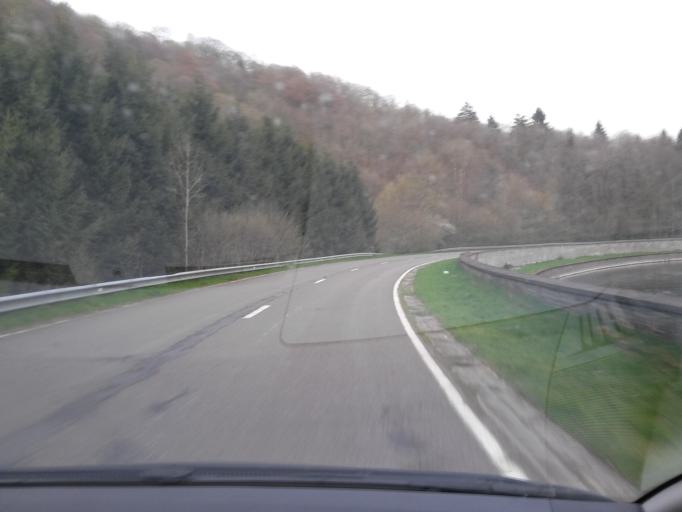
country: BE
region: Wallonia
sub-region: Province du Luxembourg
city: Herbeumont
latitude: 49.7962
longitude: 5.2254
